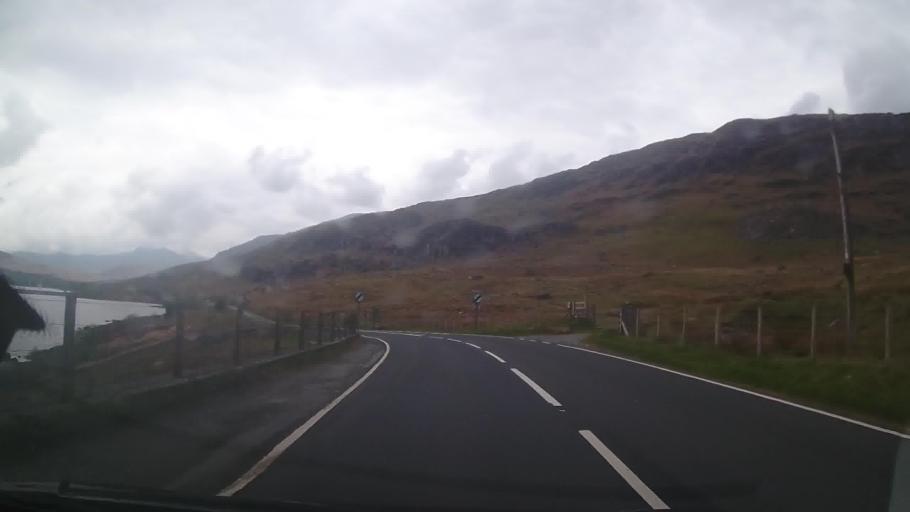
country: GB
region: Wales
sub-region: Gwynedd
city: Blaenau-Ffestiniog
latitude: 53.1021
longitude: -3.9208
